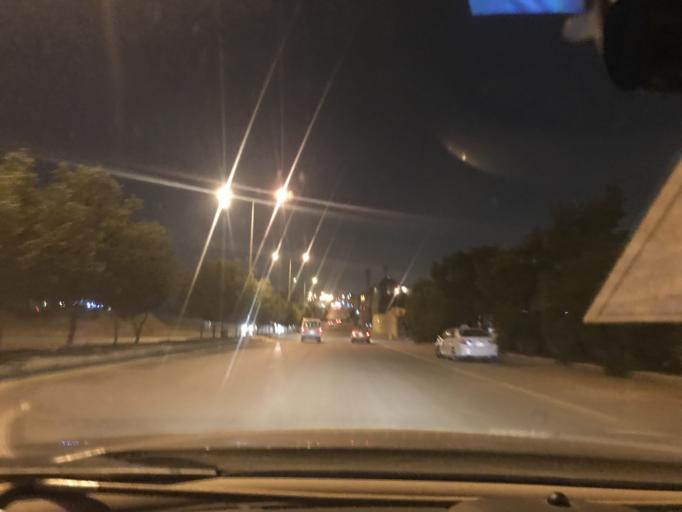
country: SA
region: Ar Riyad
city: Riyadh
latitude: 24.7534
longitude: 46.7545
